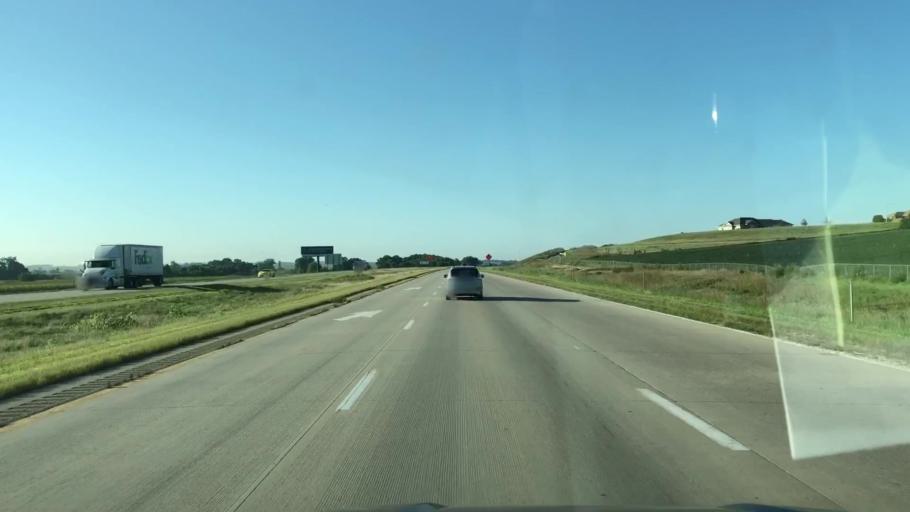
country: US
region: Iowa
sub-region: Plymouth County
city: Le Mars
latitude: 42.7594
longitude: -96.2095
